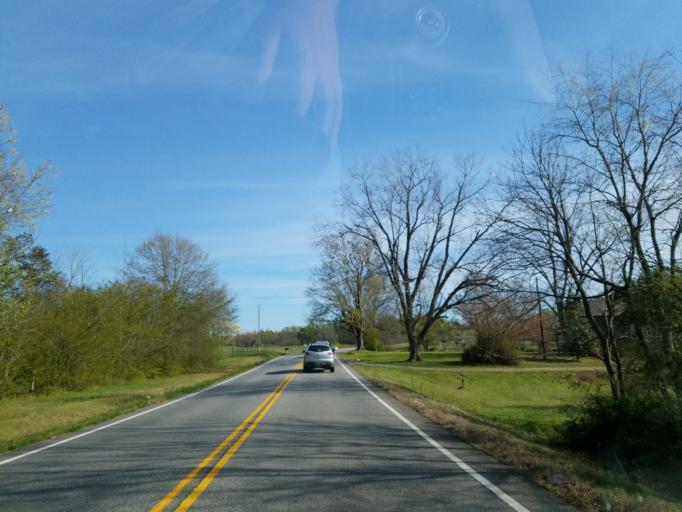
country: US
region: Georgia
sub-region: Dawson County
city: Dawsonville
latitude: 34.4555
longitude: -84.0892
